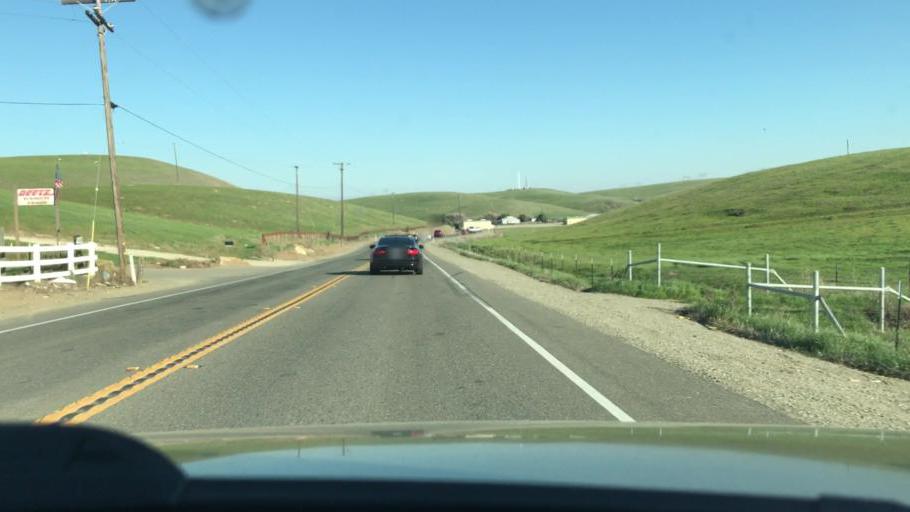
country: US
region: California
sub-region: San Joaquin County
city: Mountain House
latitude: 37.7448
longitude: -121.5966
